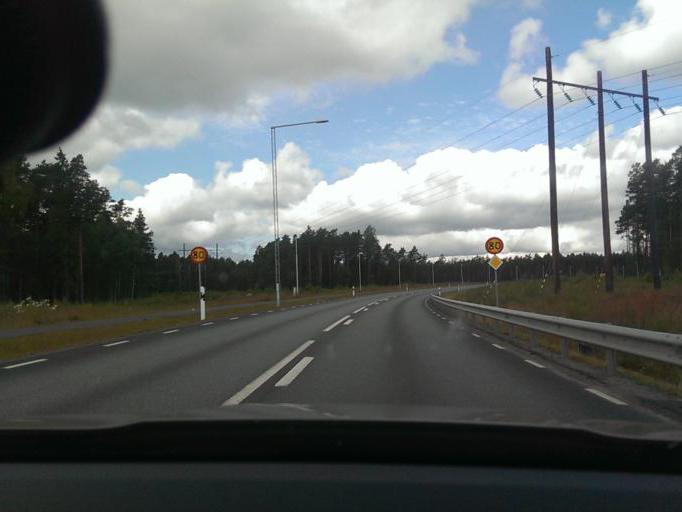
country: SE
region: Joenkoeping
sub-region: Varnamo Kommun
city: Varnamo
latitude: 57.1935
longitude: 14.0631
